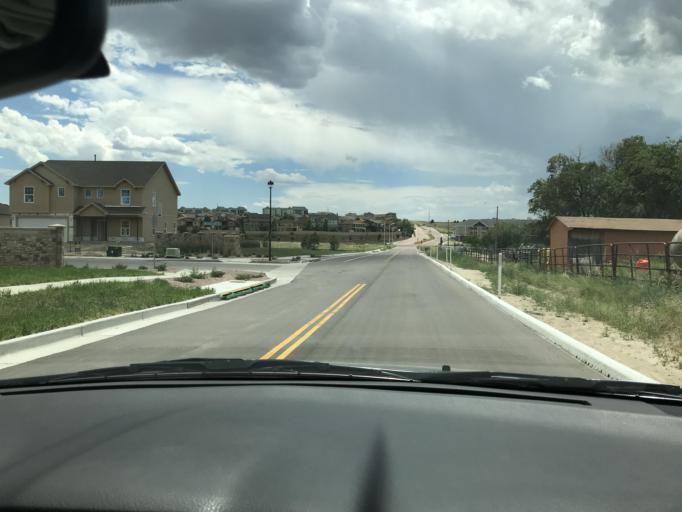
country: US
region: Colorado
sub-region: El Paso County
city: Black Forest
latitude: 38.9526
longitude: -104.7145
